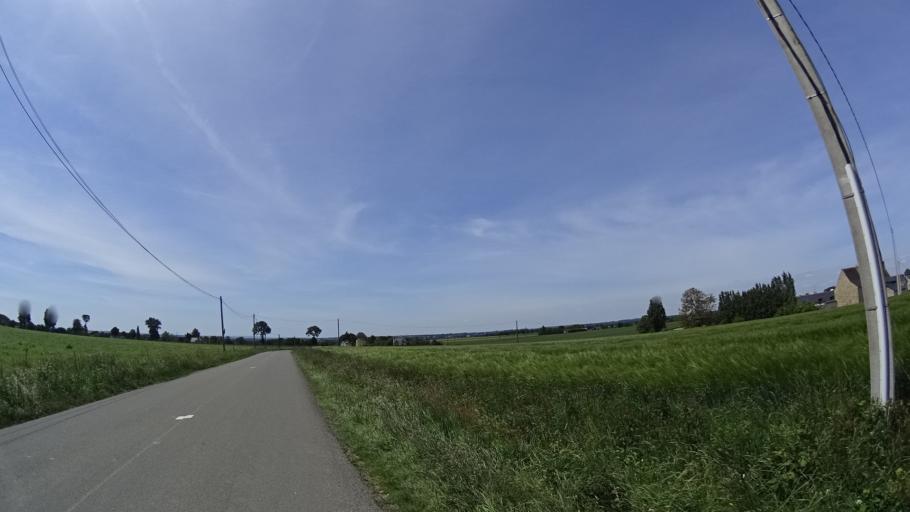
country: FR
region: Brittany
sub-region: Departement d'Ille-et-Vilaine
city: Romille
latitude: 48.1956
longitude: -1.8606
